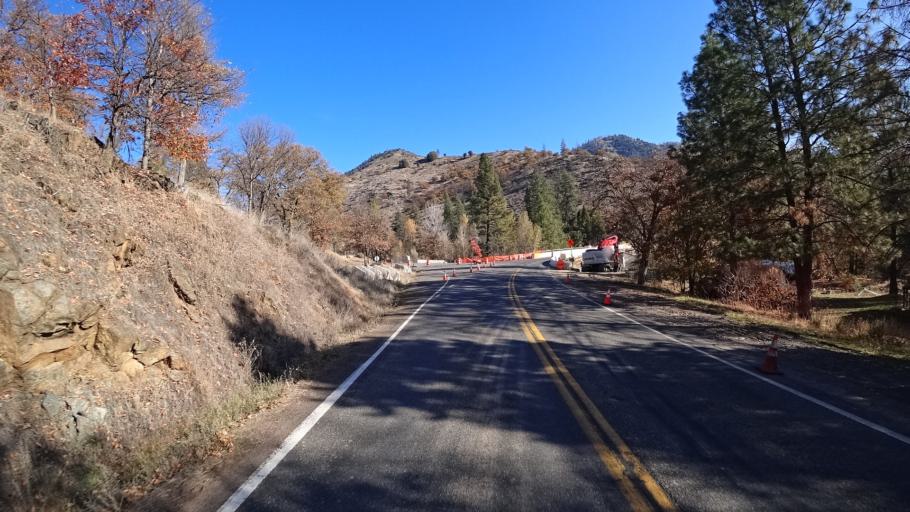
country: US
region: California
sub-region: Siskiyou County
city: Yreka
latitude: 41.8697
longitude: -122.8181
